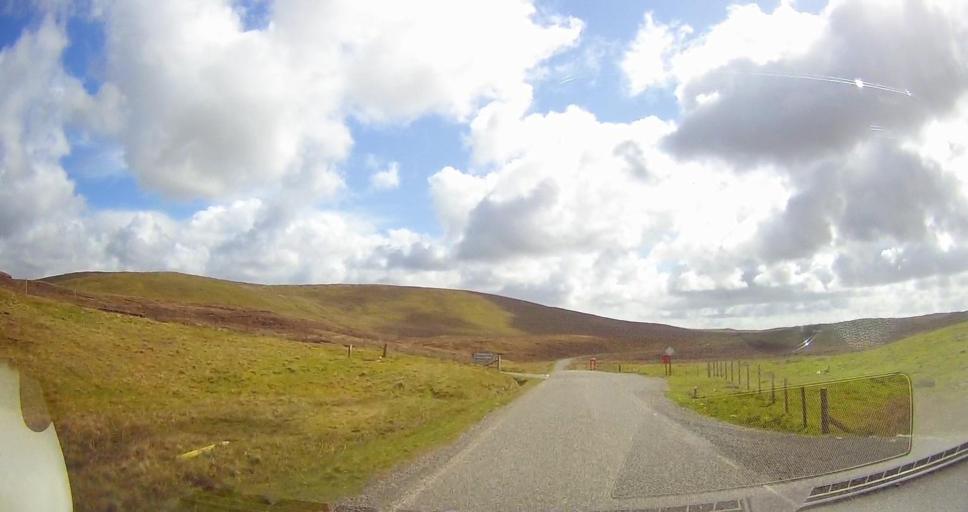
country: GB
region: Scotland
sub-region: Shetland Islands
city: Lerwick
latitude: 60.5199
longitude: -1.3772
